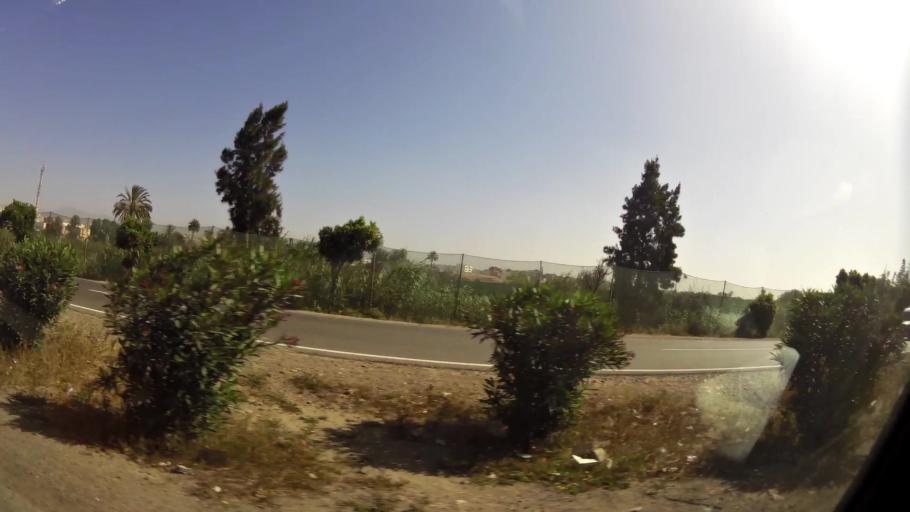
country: MA
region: Souss-Massa-Draa
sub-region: Inezgane-Ait Mellou
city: Inezgane
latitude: 30.3690
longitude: -9.4992
